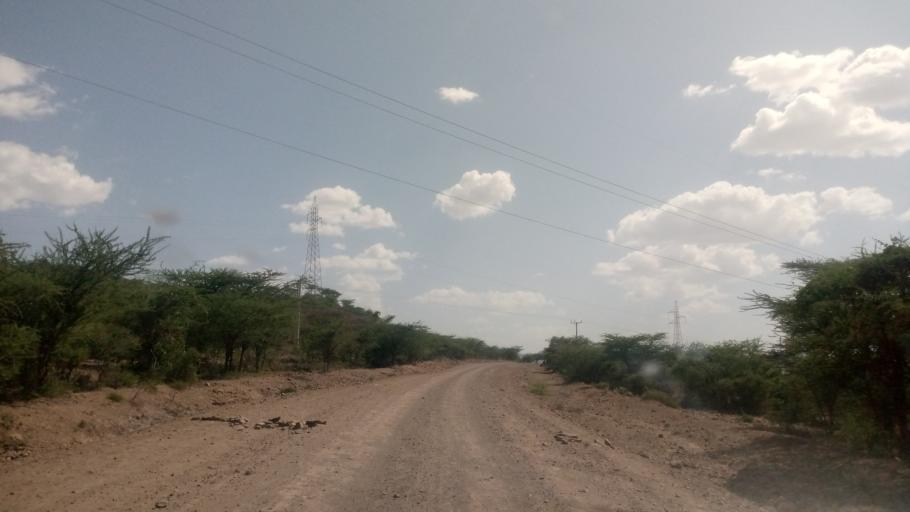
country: ET
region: Oromiya
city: Deder
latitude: 9.5246
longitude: 41.2258
